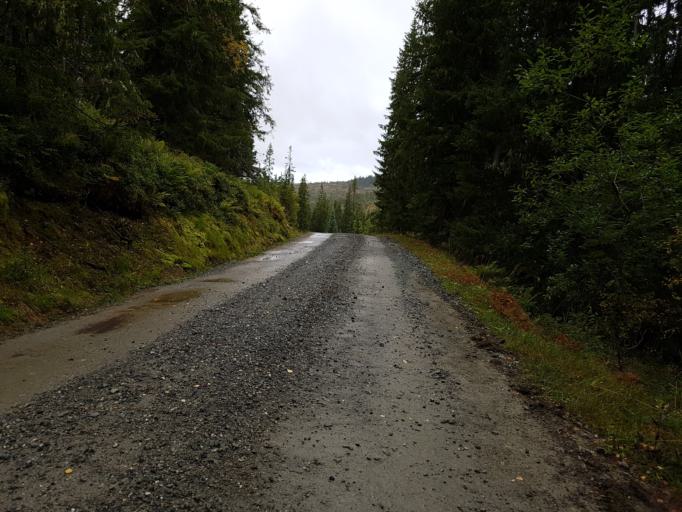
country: NO
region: Sor-Trondelag
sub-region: Melhus
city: Melhus
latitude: 63.4133
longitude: 10.2490
